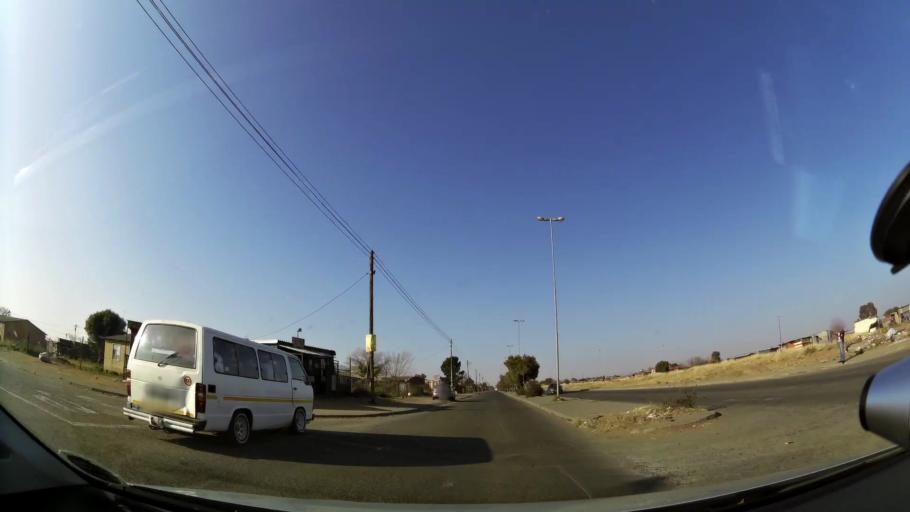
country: ZA
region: Orange Free State
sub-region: Mangaung Metropolitan Municipality
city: Bloemfontein
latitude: -29.1492
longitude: 26.2510
